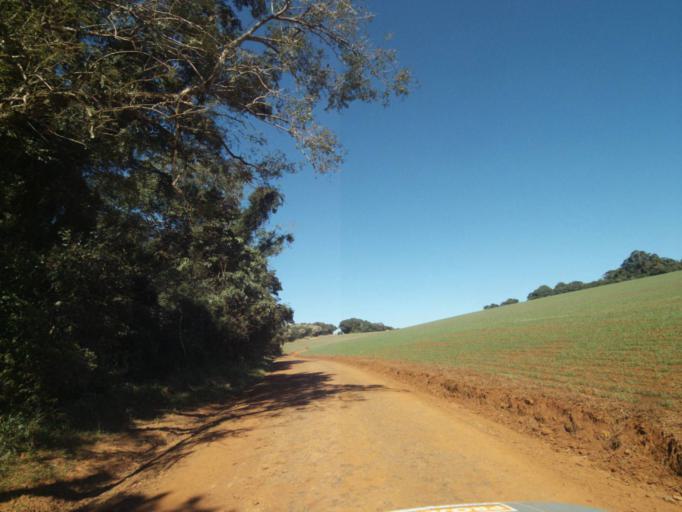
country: BR
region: Parana
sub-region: Tibagi
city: Tibagi
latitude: -24.5685
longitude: -50.6273
